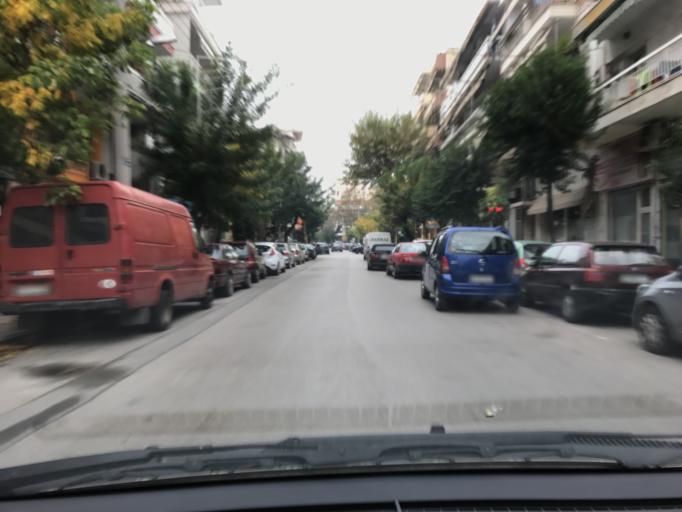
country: GR
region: Central Macedonia
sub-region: Nomos Thessalonikis
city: Ampelokipoi
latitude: 40.6528
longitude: 22.9261
